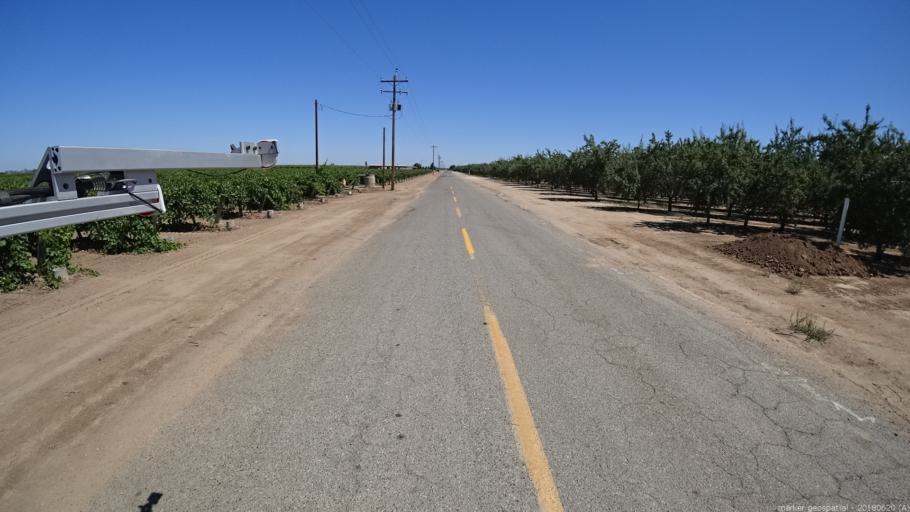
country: US
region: California
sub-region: Madera County
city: Parkwood
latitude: 36.8965
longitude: -120.0015
